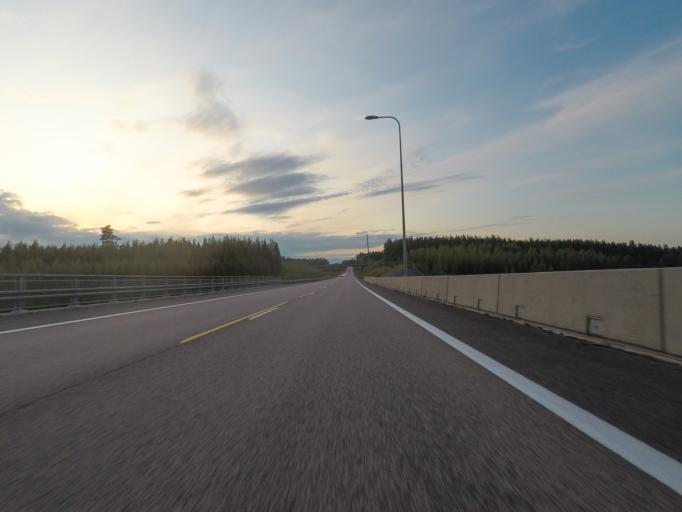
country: FI
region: Central Finland
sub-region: Jyvaeskylae
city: Toivakka
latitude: 62.1028
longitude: 25.9830
